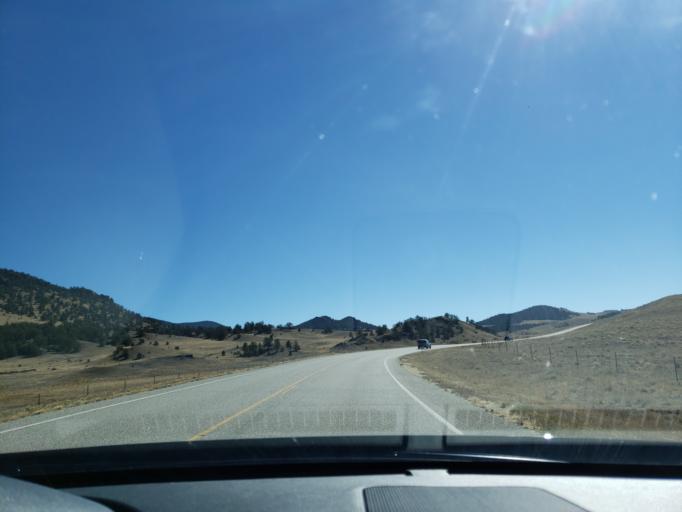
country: US
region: Colorado
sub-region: Chaffee County
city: Salida
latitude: 38.8594
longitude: -105.6549
